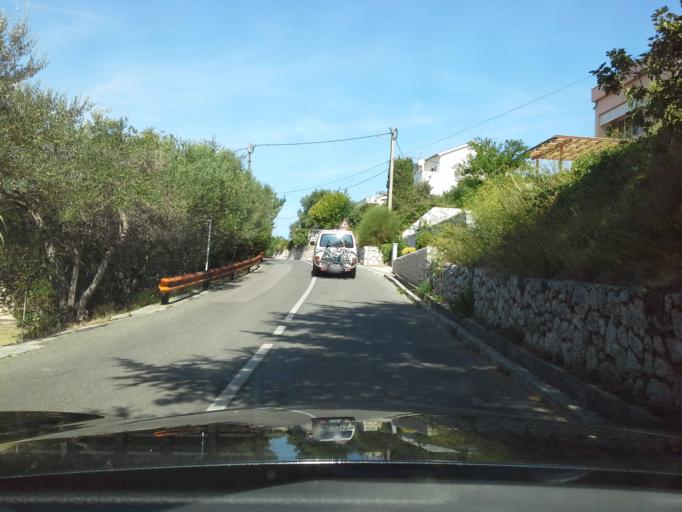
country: HR
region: Primorsko-Goranska
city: Banjol
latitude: 44.7553
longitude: 14.7715
